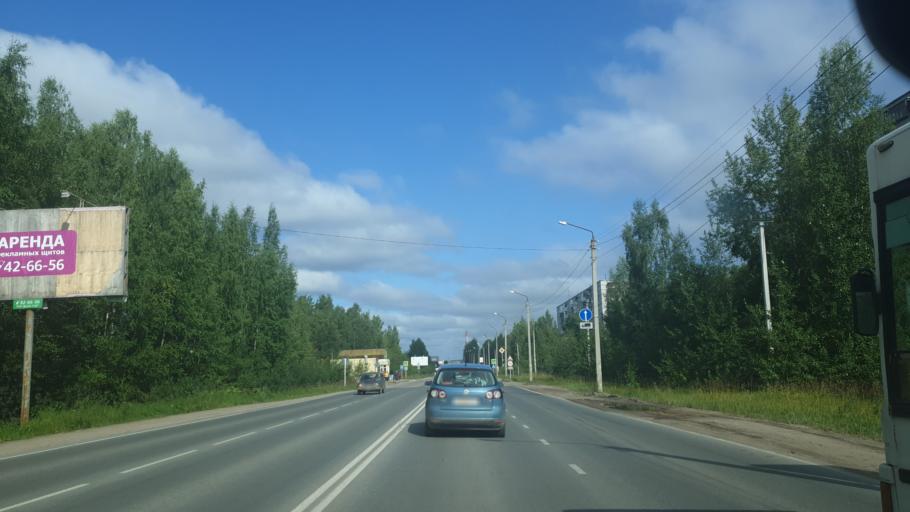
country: RU
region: Komi Republic
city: Ezhva
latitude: 61.7874
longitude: 50.7439
